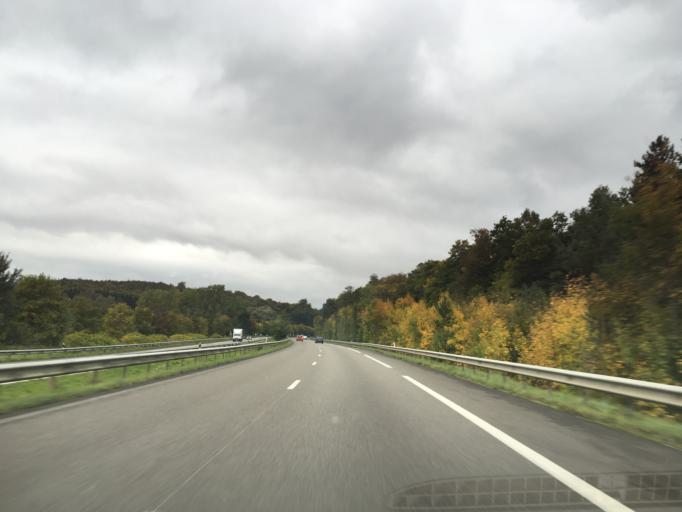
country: FR
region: Lorraine
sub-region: Departement de la Meuse
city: Vacon
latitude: 48.6878
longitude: 5.5660
